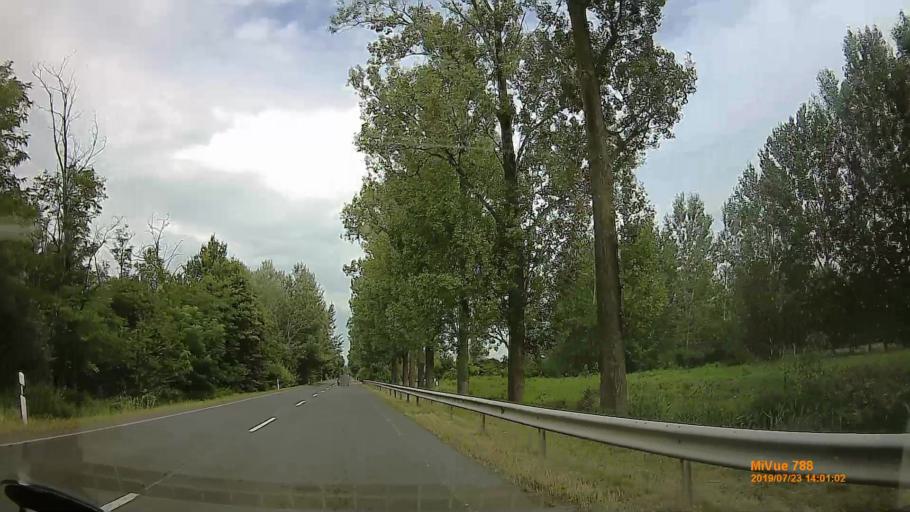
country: HU
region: Szabolcs-Szatmar-Bereg
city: Tiszavasvari
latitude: 47.9419
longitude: 21.3160
